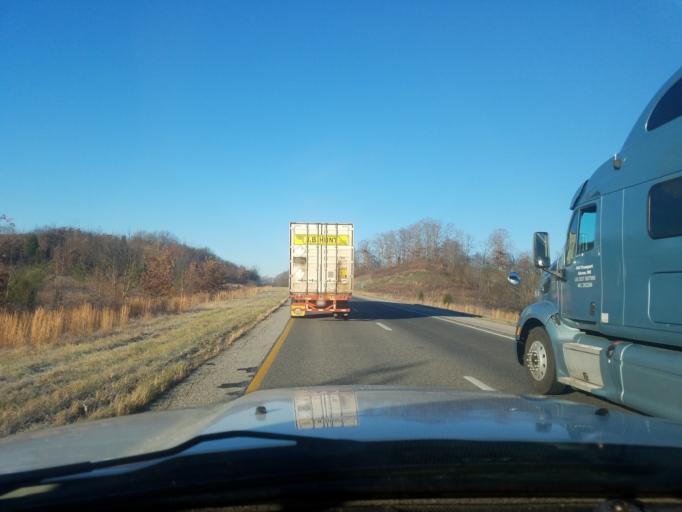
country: US
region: Indiana
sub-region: Dubois County
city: Ferdinand
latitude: 38.2128
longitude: -86.7581
